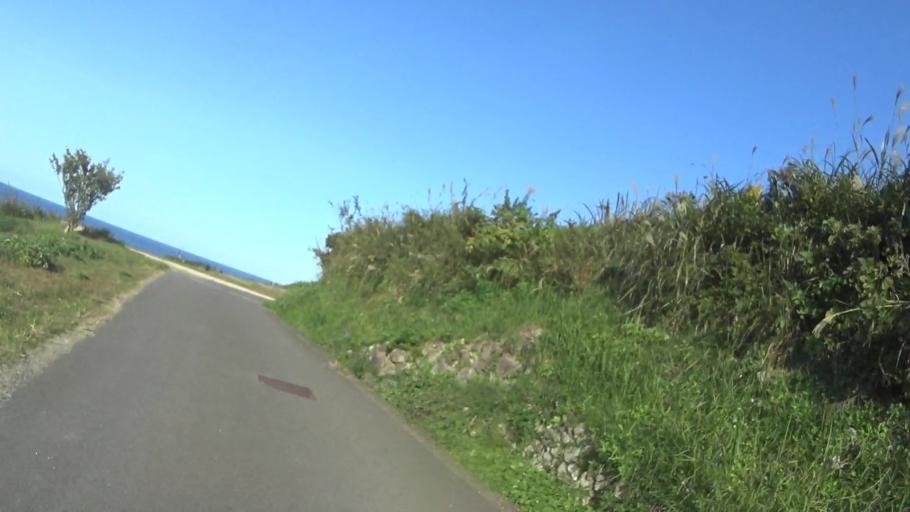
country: JP
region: Kyoto
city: Miyazu
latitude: 35.7612
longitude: 135.2069
